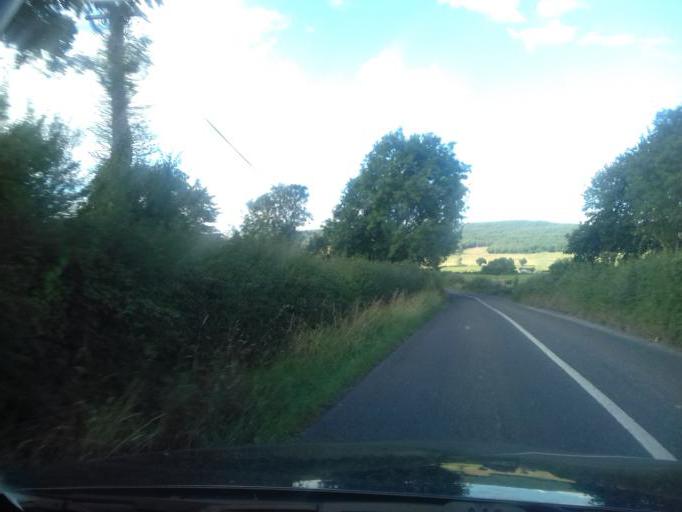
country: IE
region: Munster
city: Carrick-on-Suir
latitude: 52.3897
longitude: -7.4676
